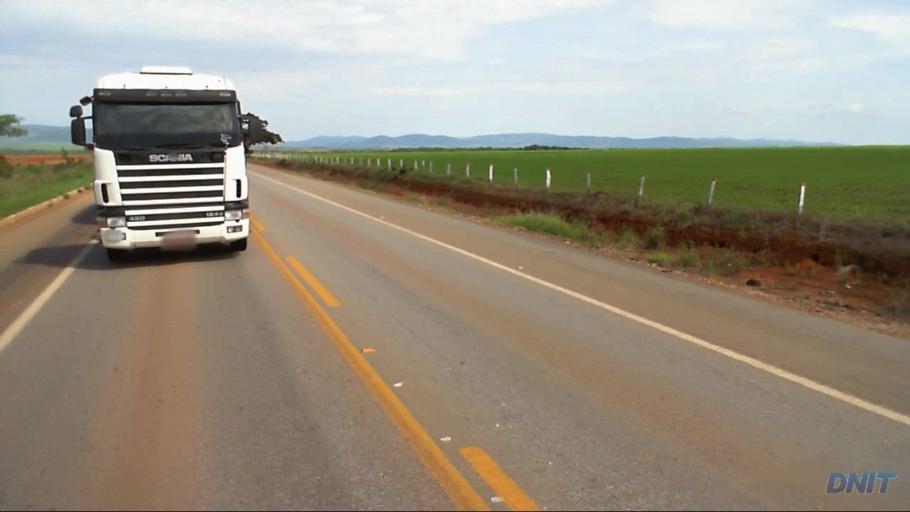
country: BR
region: Goias
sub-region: Barro Alto
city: Barro Alto
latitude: -15.1144
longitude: -48.8406
